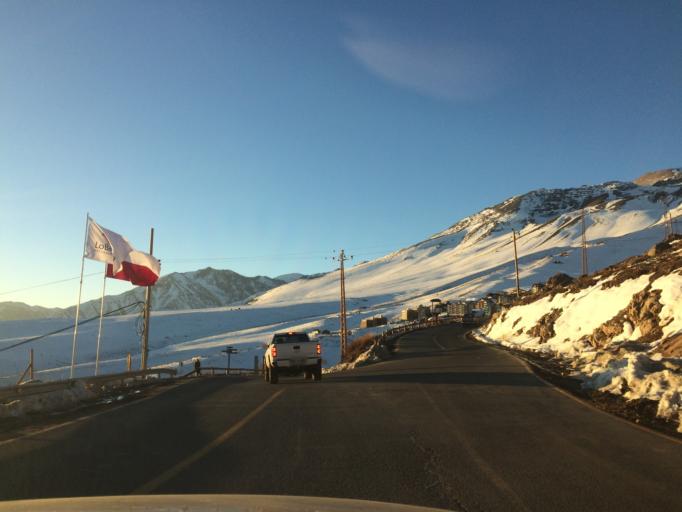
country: CL
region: Santiago Metropolitan
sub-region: Provincia de Santiago
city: Villa Presidente Frei, Nunoa, Santiago, Chile
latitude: -33.3434
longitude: -70.2948
